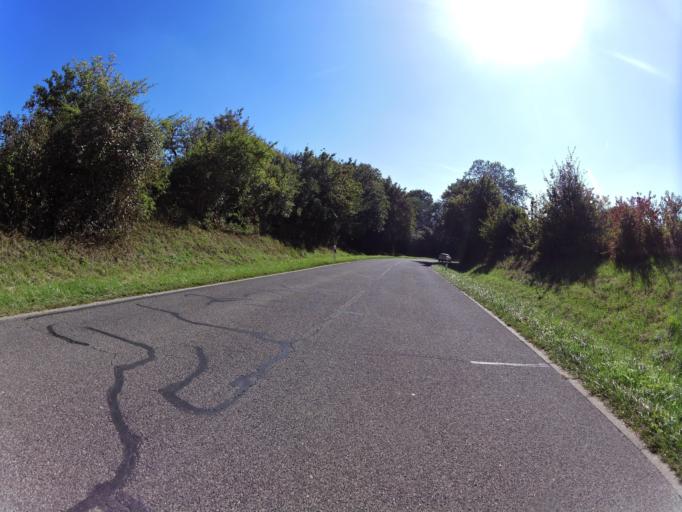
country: DE
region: Bavaria
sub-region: Regierungsbezirk Unterfranken
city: Kleinrinderfeld
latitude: 49.6964
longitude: 9.7887
